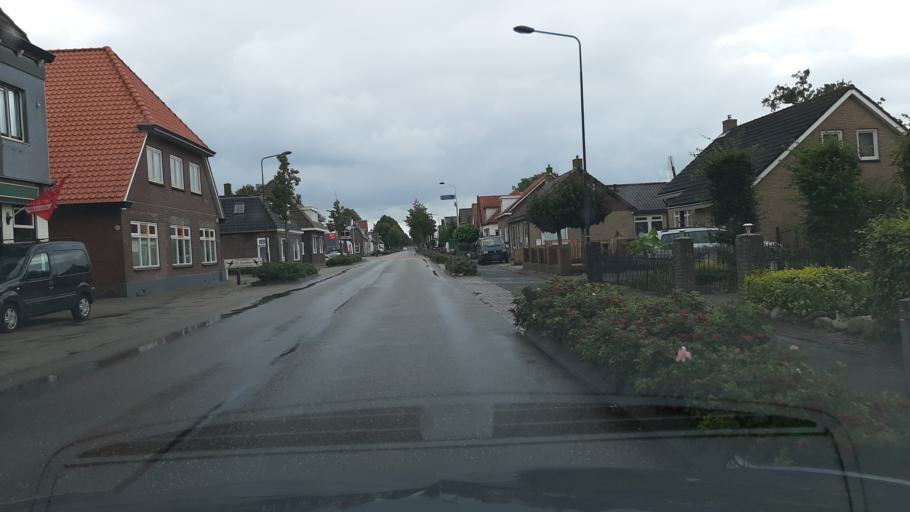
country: NL
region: Friesland
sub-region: Gemeente Weststellingwerf
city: Steggerda
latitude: 52.8450
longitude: 6.0380
